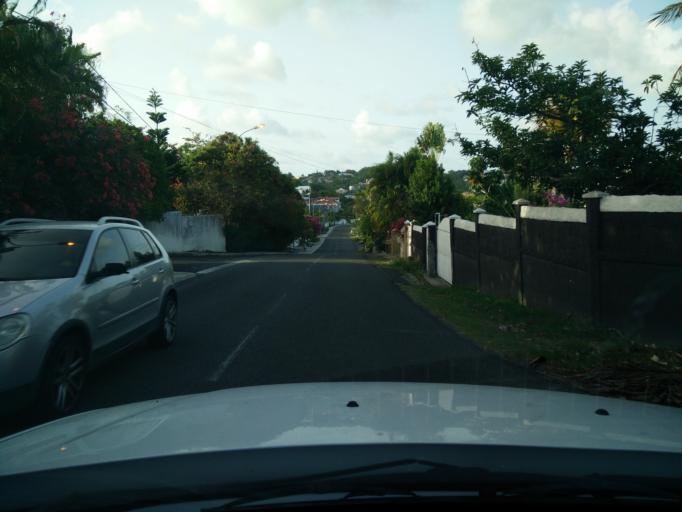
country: GP
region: Guadeloupe
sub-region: Guadeloupe
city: Le Gosier
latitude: 16.2030
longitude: -61.4720
